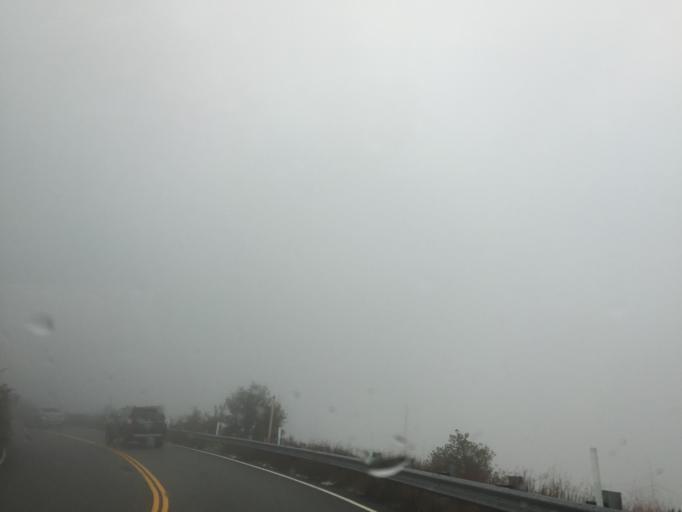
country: US
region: California
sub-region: Los Angeles County
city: Glendora
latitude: 34.2993
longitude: -117.8399
